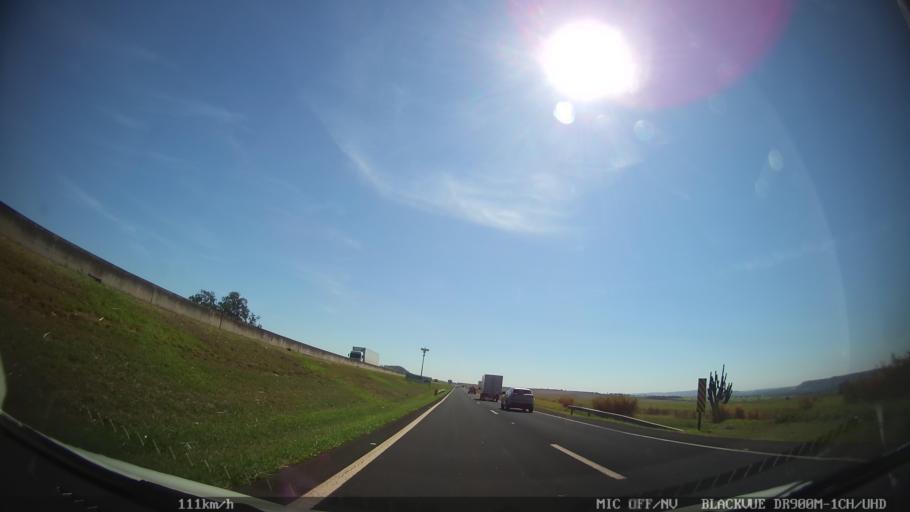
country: BR
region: Sao Paulo
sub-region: Sao Simao
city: Sao Simao
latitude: -21.4524
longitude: -47.6462
